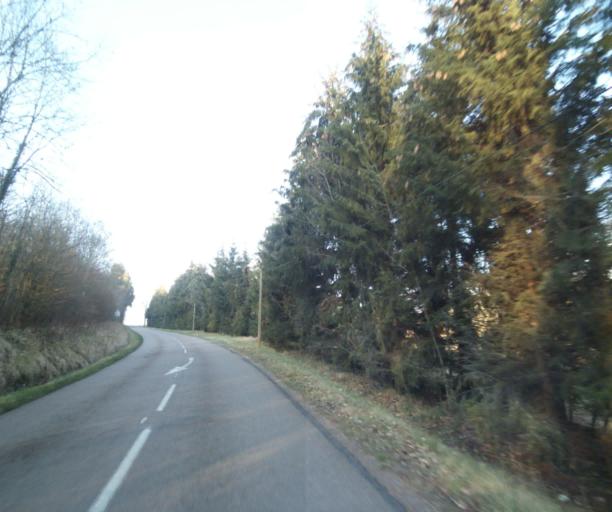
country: FR
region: Champagne-Ardenne
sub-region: Departement de la Haute-Marne
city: Bienville
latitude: 48.5565
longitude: 5.0868
